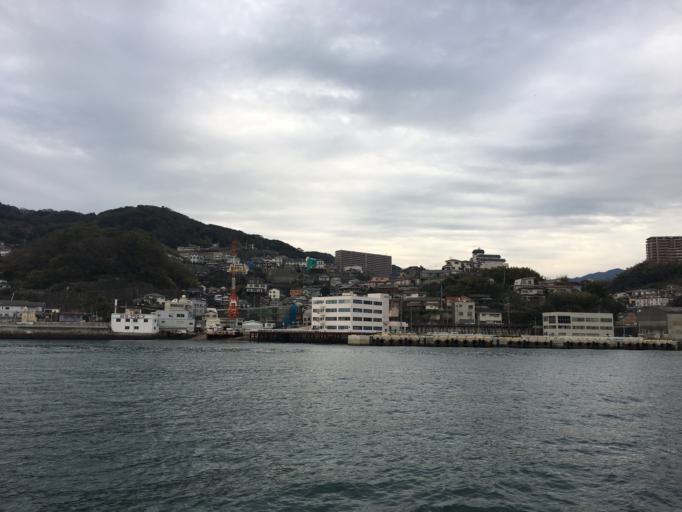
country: JP
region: Nagasaki
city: Nagasaki-shi
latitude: 32.7309
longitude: 129.8601
